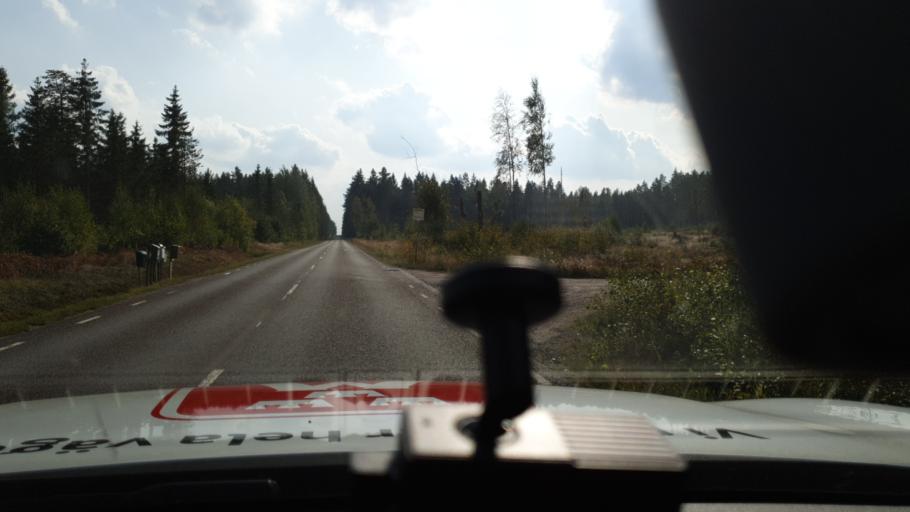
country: SE
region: Kalmar
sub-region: Vimmerby Kommun
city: Vimmerby
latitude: 57.6971
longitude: 15.8432
